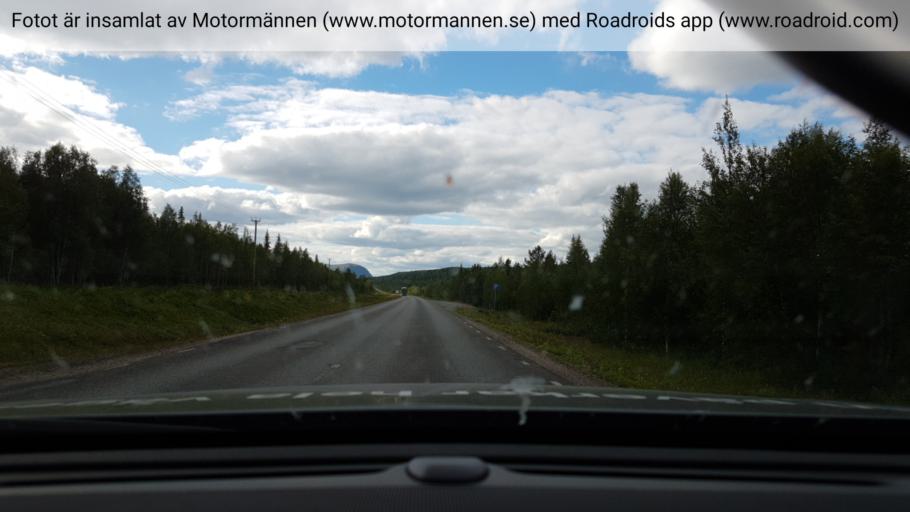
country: SE
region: Norrbotten
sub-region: Arjeplogs Kommun
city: Arjeplog
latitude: 66.2952
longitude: 17.1721
